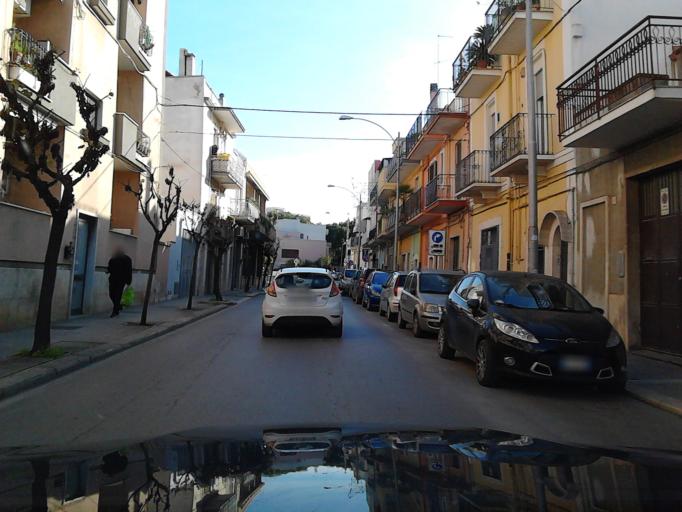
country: IT
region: Apulia
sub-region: Provincia di Bari
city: Rutigliano
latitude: 41.0128
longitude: 17.0023
